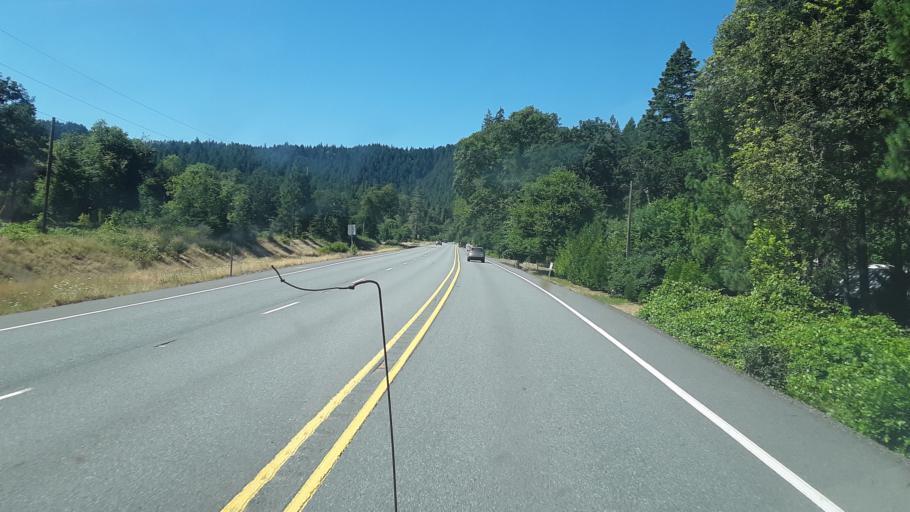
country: US
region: Oregon
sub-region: Josephine County
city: Redwood
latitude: 42.3693
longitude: -123.5063
